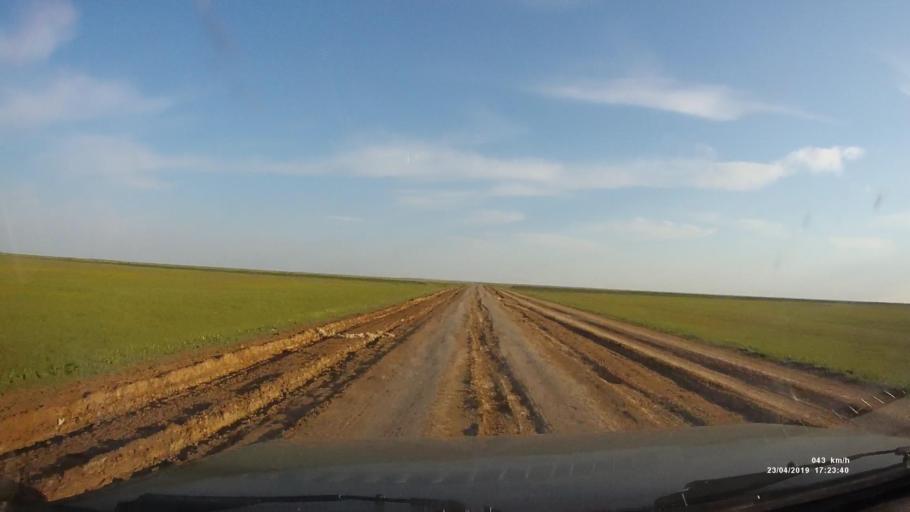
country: RU
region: Kalmykiya
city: Priyutnoye
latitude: 46.1609
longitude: 43.5079
